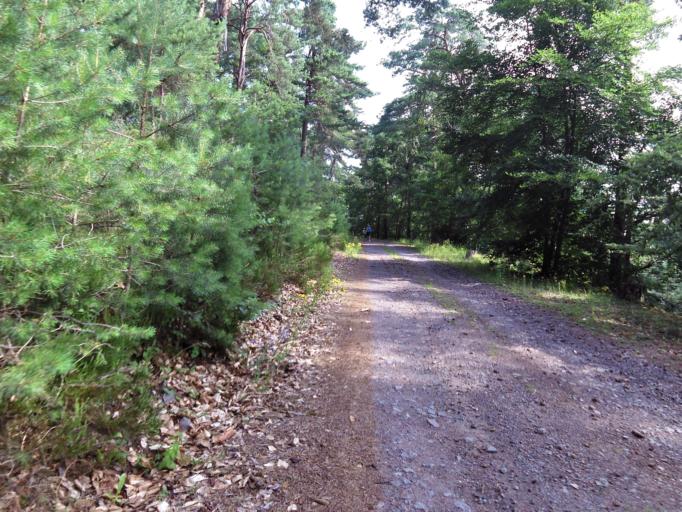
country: DE
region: Rheinland-Pfalz
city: Bad Duerkheim
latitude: 49.4479
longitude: 8.1261
